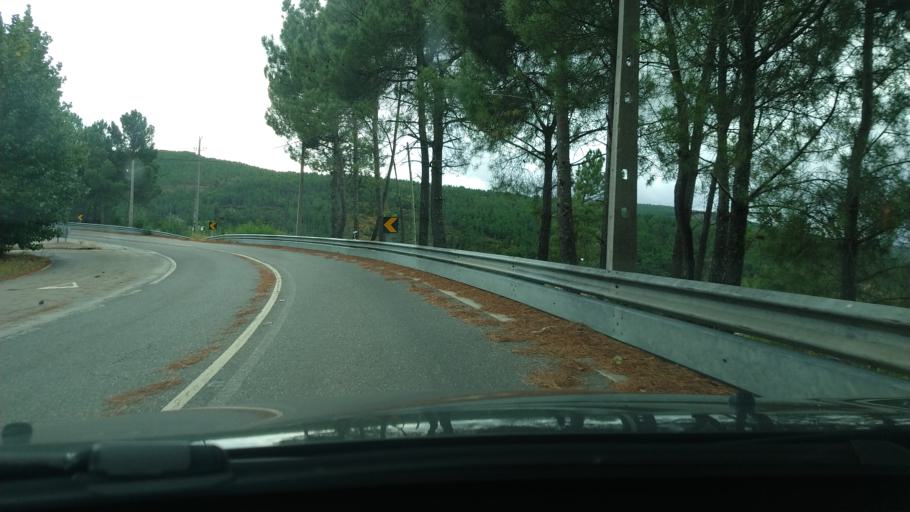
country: PT
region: Castelo Branco
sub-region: Covilha
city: Covilha
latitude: 40.2385
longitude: -7.5919
